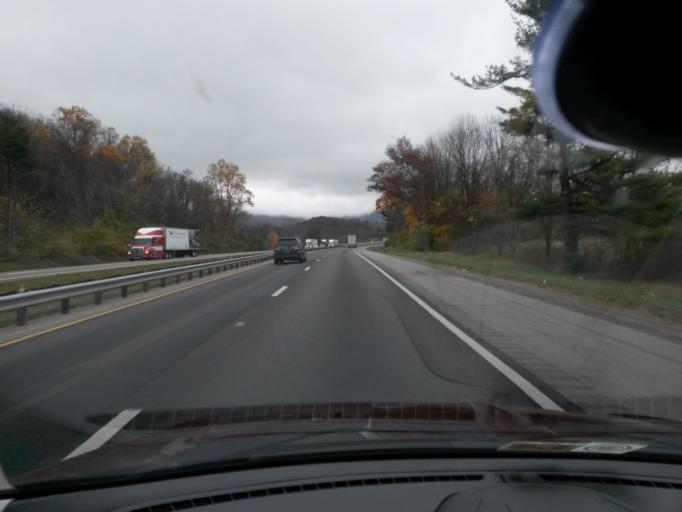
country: US
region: Virginia
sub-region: Pulaski County
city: Pulaski
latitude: 36.9871
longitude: -80.8194
